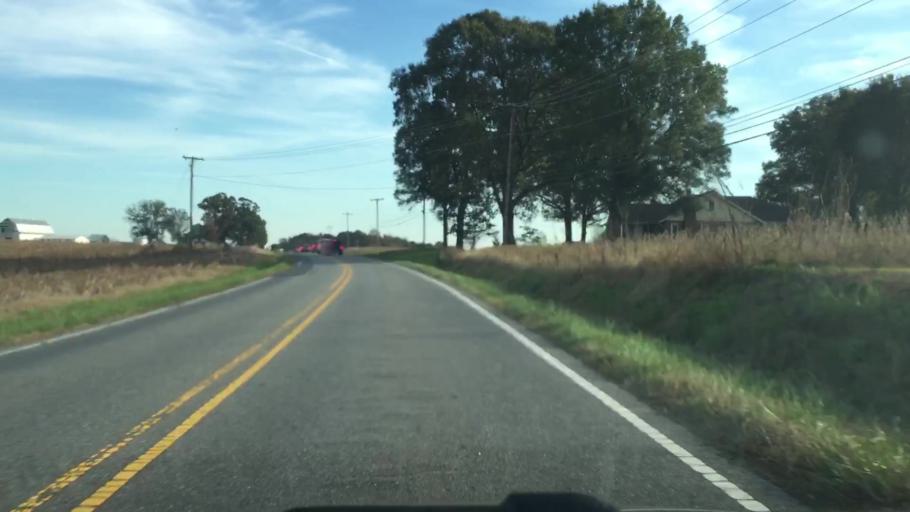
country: US
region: North Carolina
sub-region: Iredell County
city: Mooresville
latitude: 35.5656
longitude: -80.7911
